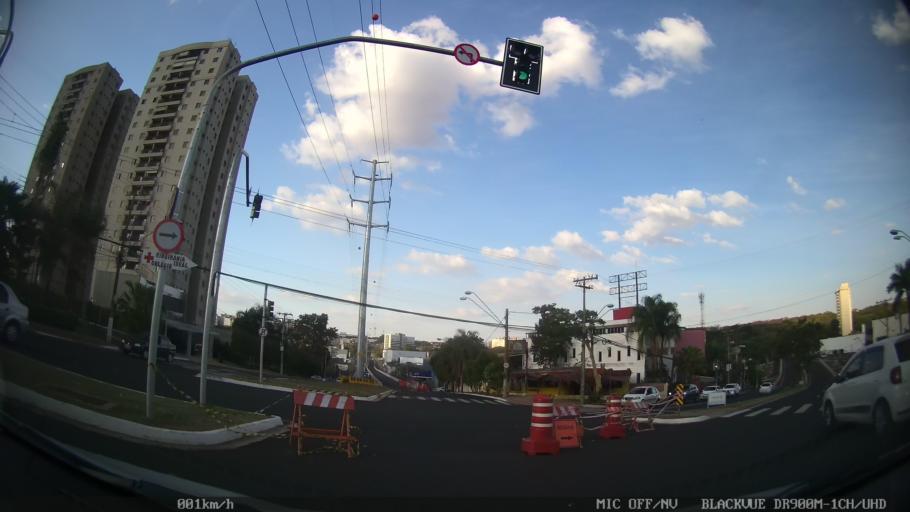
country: BR
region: Sao Paulo
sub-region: Ribeirao Preto
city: Ribeirao Preto
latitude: -21.1933
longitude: -47.8001
